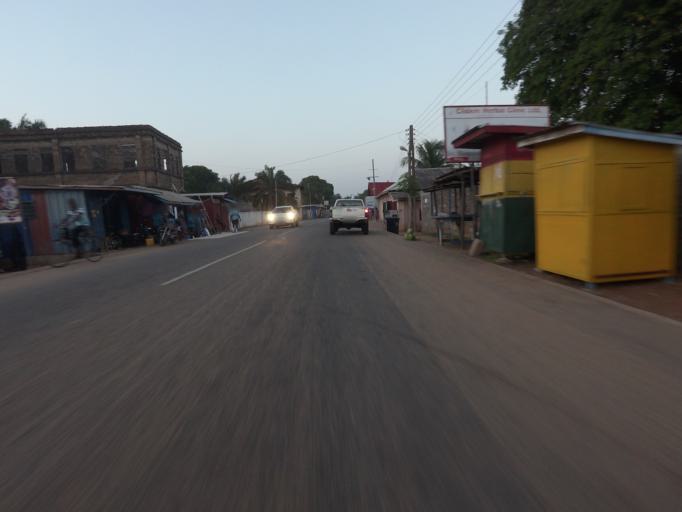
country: GH
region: Volta
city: Keta
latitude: 5.8932
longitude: 0.9858
